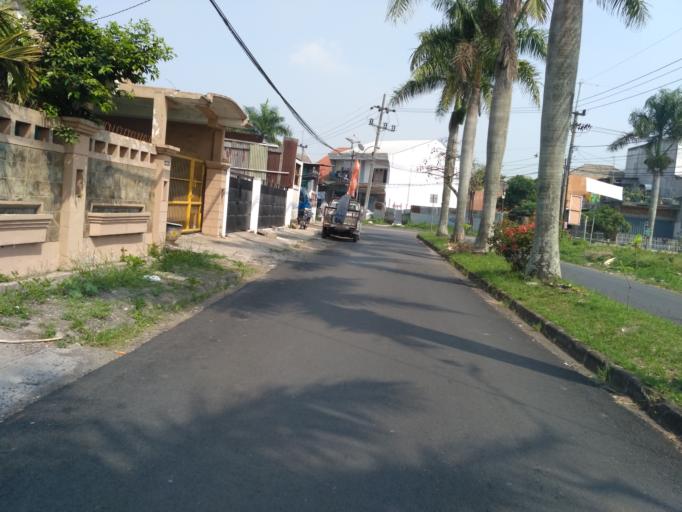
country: ID
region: East Java
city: Malang
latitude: -7.9663
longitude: 112.6662
